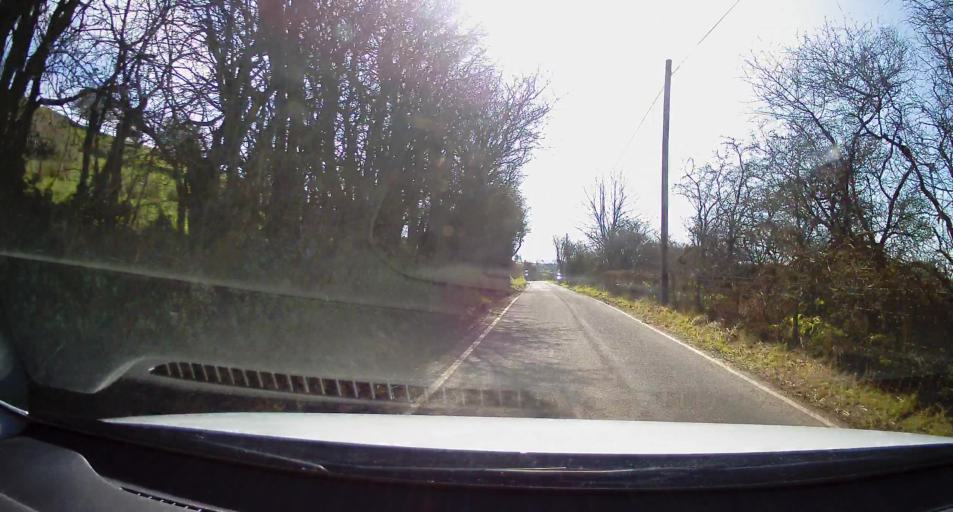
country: GB
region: Wales
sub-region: County of Ceredigion
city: Lledrod
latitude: 52.2819
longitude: -4.0606
